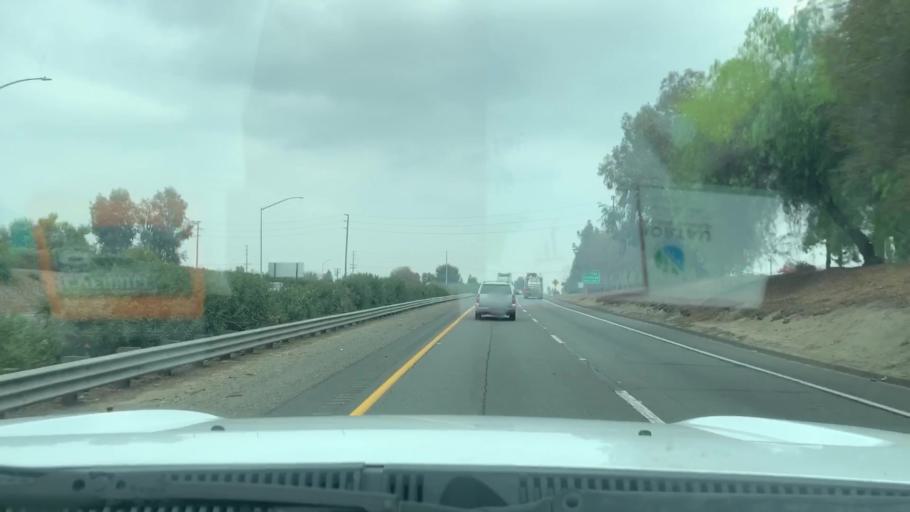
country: US
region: California
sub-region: Tulare County
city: Tulare
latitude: 36.2233
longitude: -119.3333
